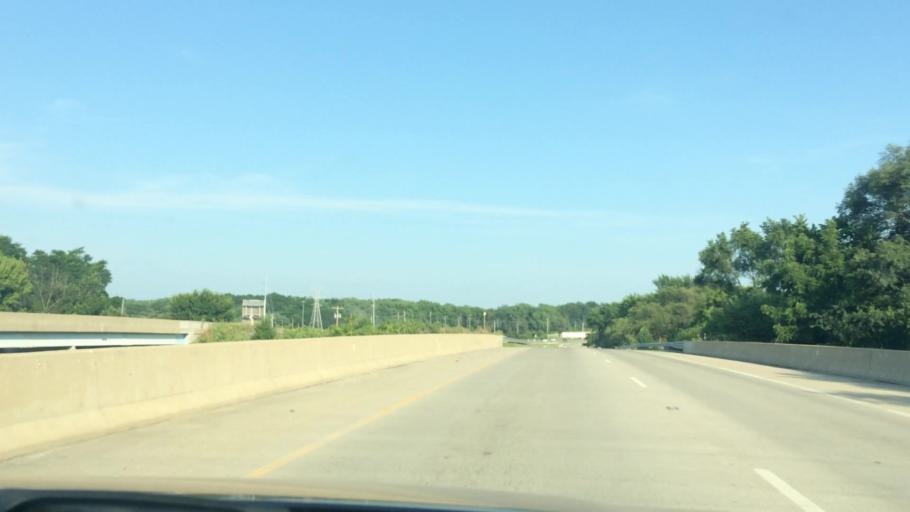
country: US
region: Indiana
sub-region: Tippecanoe County
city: Lafayette
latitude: 40.4416
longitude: -86.8648
